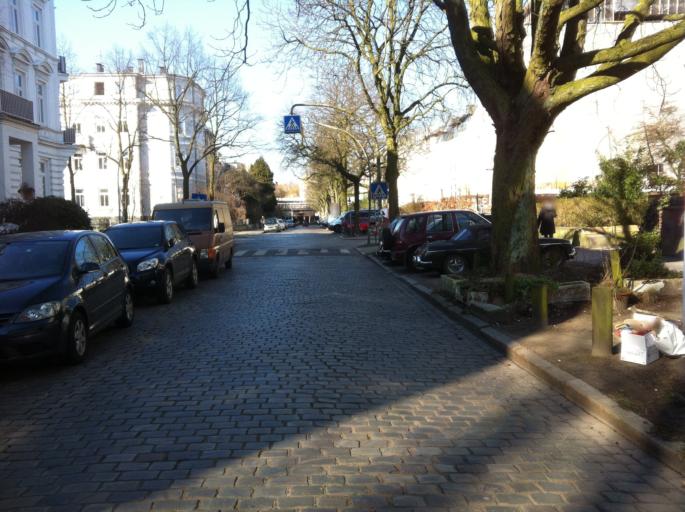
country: DE
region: Hamburg
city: St. Pauli
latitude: 53.5592
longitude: 9.9549
